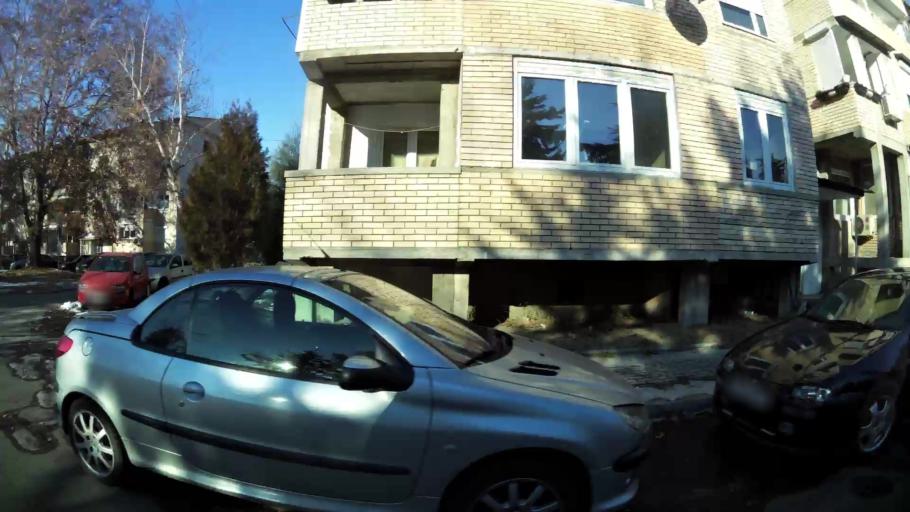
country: MK
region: Karpos
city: Skopje
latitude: 42.0048
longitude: 21.4010
